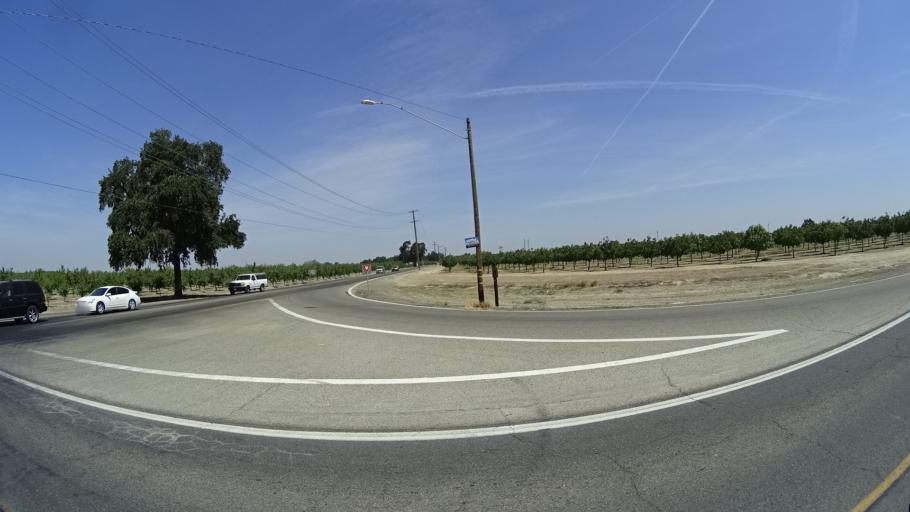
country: US
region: California
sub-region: Kings County
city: Lucerne
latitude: 36.4012
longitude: -119.6864
